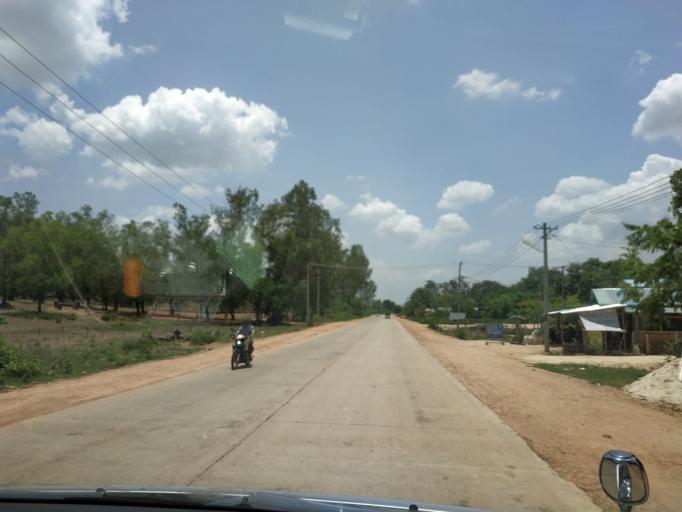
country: MM
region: Bago
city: Bago
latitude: 17.4720
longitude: 96.4713
